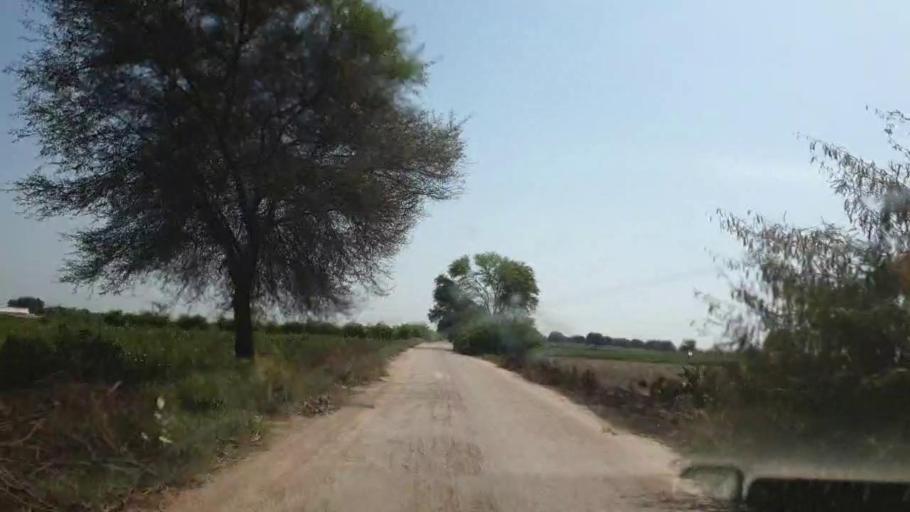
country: PK
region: Sindh
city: Tando Jam
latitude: 25.3958
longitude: 68.5870
